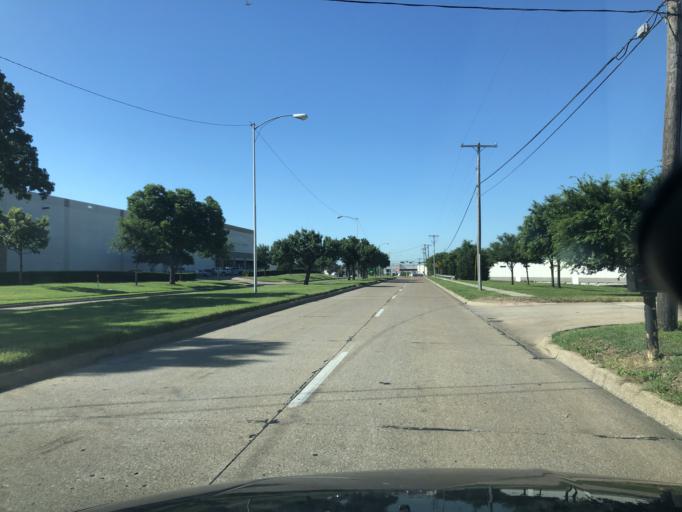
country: US
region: Texas
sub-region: Tarrant County
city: Euless
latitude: 32.8055
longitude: -97.0302
